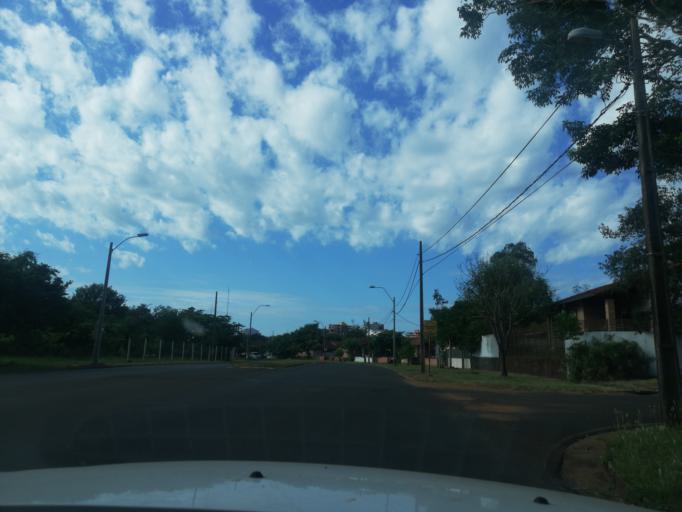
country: PY
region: Itapua
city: Encarnacion
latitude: -27.3530
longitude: -55.8491
